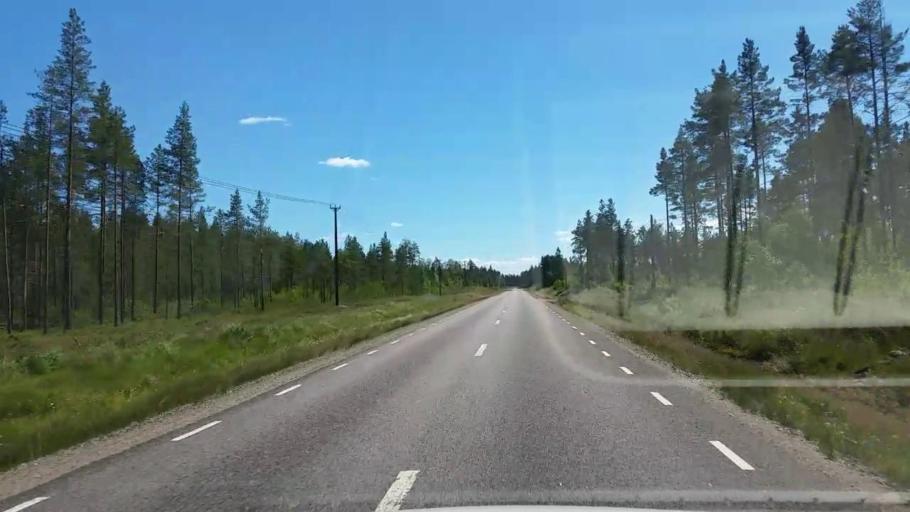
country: SE
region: Gaevleborg
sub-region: Ovanakers Kommun
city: Edsbyn
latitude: 61.4682
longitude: 15.6963
